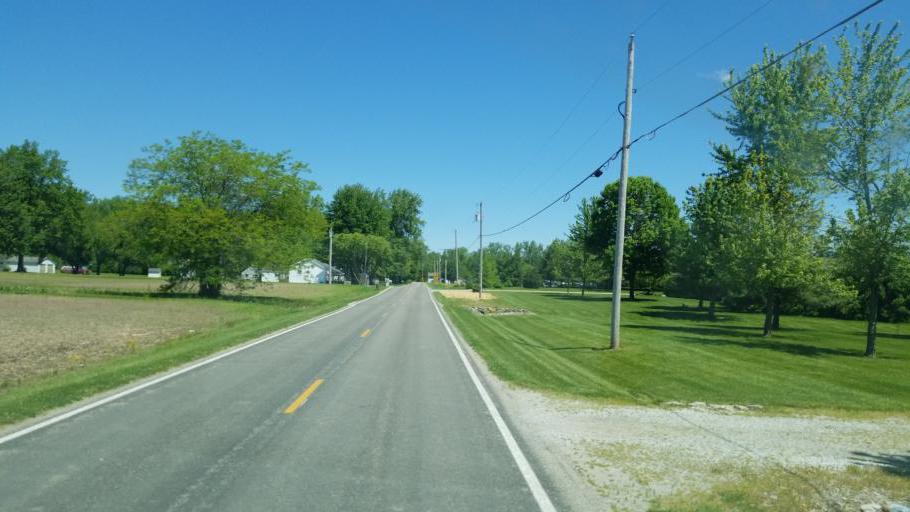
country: US
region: Ohio
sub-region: Shelby County
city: Fort Loramie
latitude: 40.3631
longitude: -84.3385
